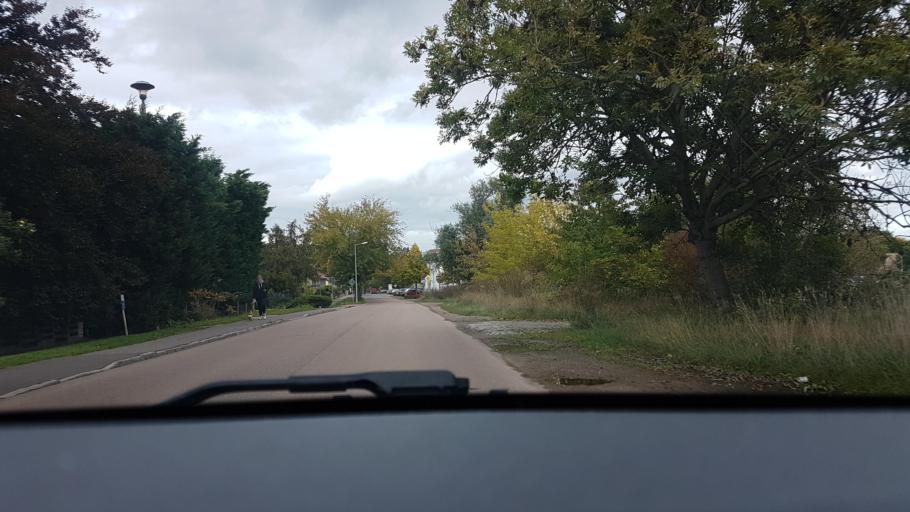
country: DE
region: Saxony-Anhalt
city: Bernburg
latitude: 51.7793
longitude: 11.7347
